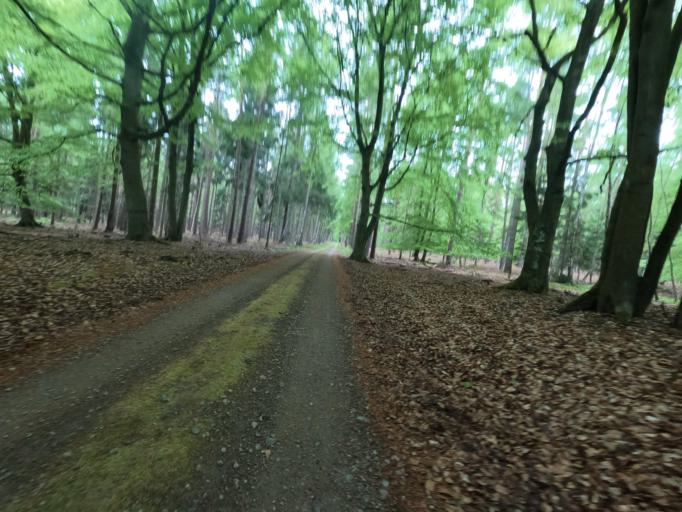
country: DE
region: Mecklenburg-Vorpommern
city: Born
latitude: 54.4141
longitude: 12.4965
